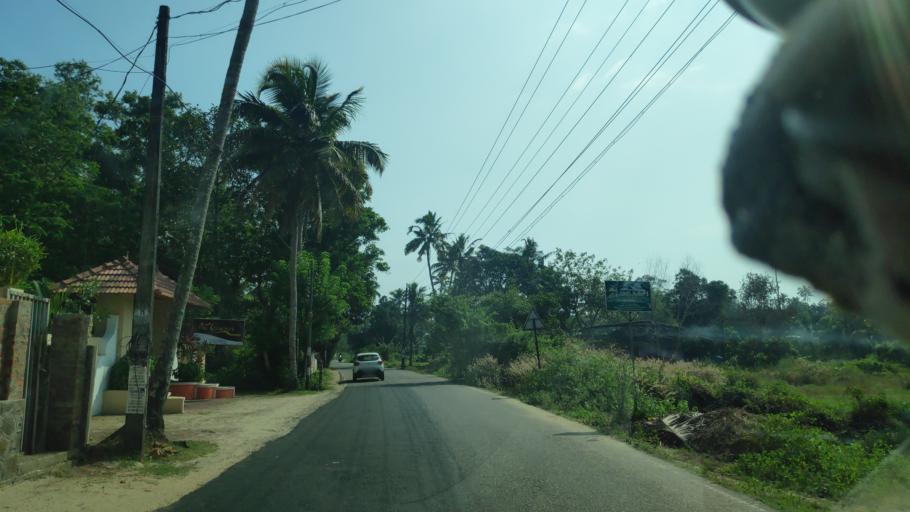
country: IN
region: Kerala
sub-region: Alappuzha
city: Shertallai
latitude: 9.6210
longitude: 76.3004
